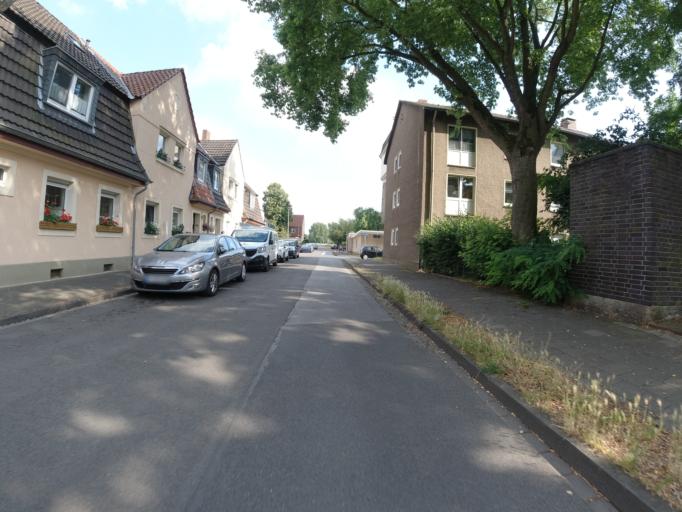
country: DE
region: North Rhine-Westphalia
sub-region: Regierungsbezirk Dusseldorf
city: Hochfeld
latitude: 51.3787
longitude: 6.6820
